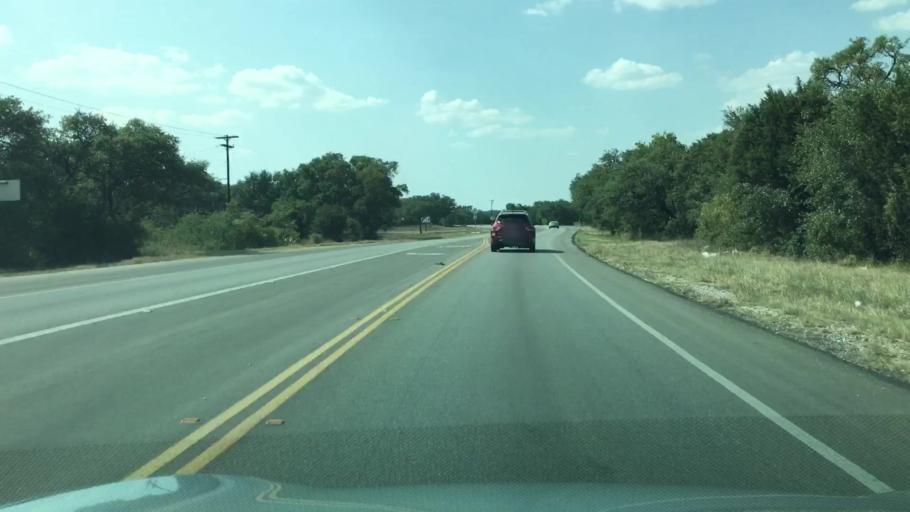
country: US
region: Texas
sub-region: Hays County
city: Wimberley
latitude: 29.9353
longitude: -98.0790
